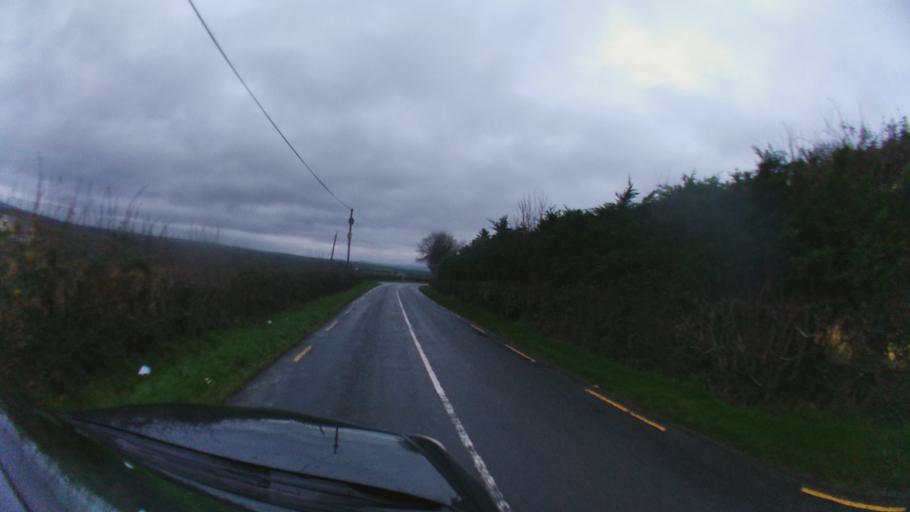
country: IE
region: Leinster
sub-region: Kilkenny
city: Graiguenamanagh
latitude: 52.5985
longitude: -6.9908
